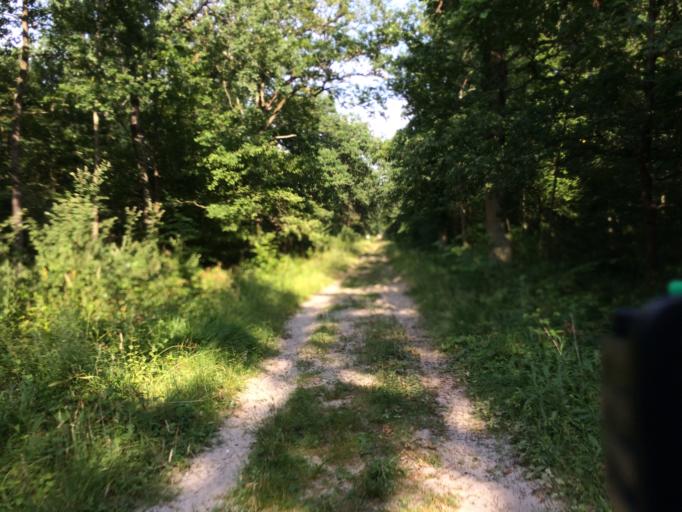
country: FR
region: Ile-de-France
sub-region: Departement de l'Essonne
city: Brunoy
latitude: 48.6673
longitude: 2.4822
